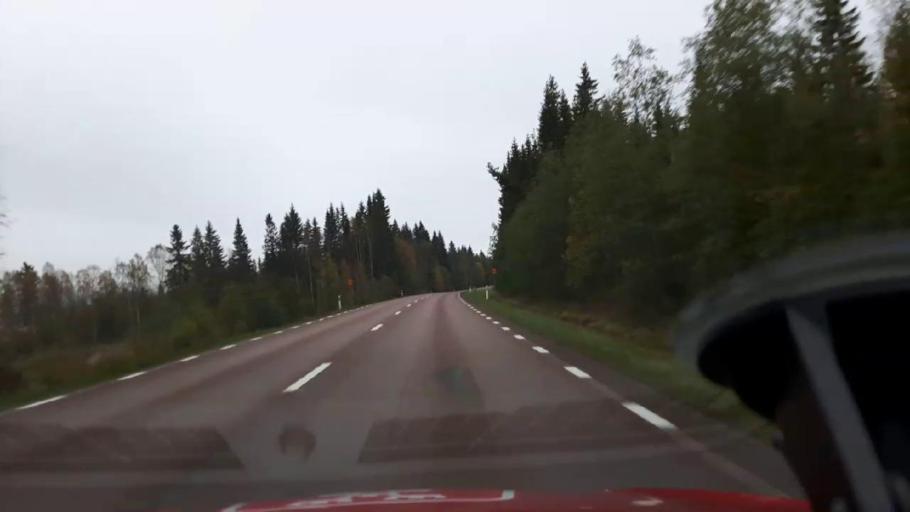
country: SE
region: Jaemtland
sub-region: Bergs Kommun
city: Hoverberg
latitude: 62.5775
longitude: 14.4472
